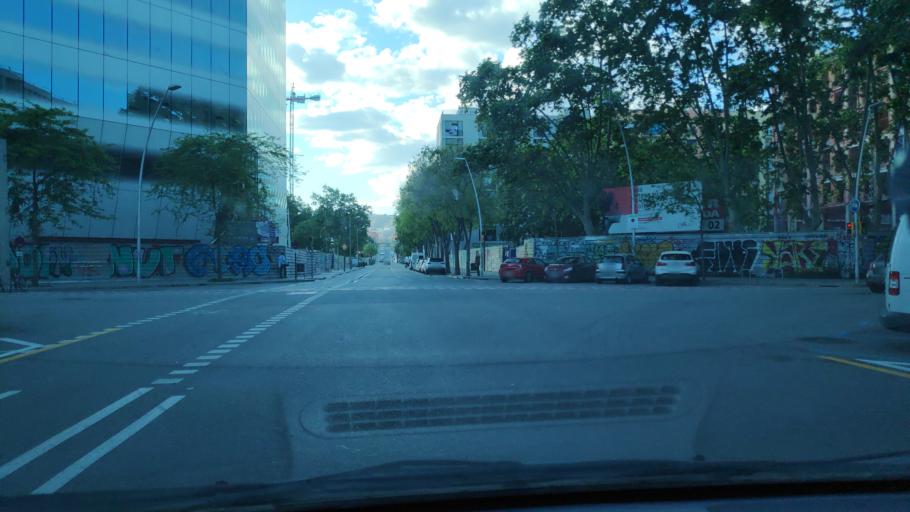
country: ES
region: Catalonia
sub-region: Provincia de Barcelona
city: Sant Marti
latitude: 41.3989
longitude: 2.1906
